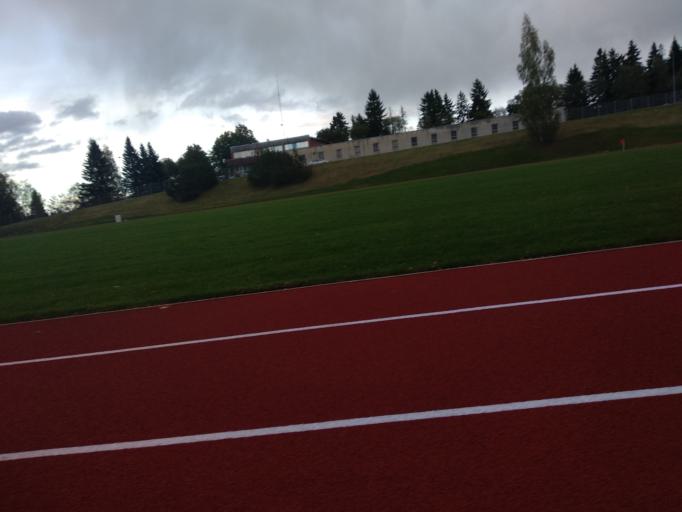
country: EE
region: Polvamaa
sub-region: Polva linn
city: Polva
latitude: 58.0499
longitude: 27.0531
